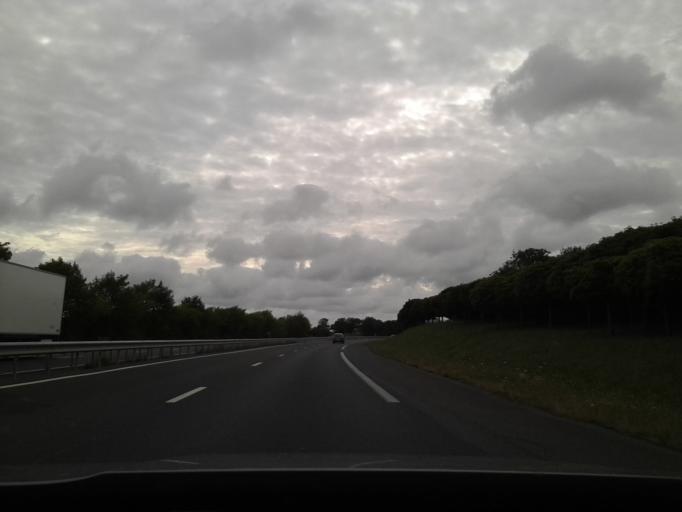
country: FR
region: Lower Normandy
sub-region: Departement du Calvados
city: Grandcamp-Maisy
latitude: 49.3436
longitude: -1.0249
